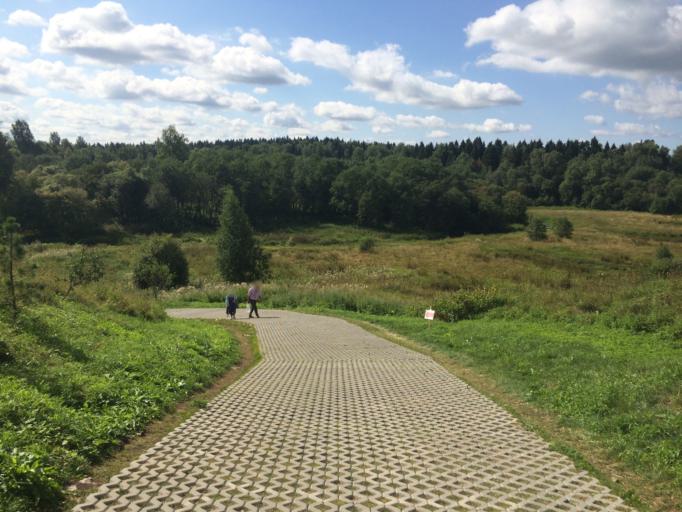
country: RU
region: Moskovskaya
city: Khot'kovo
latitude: 56.2084
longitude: 38.0374
